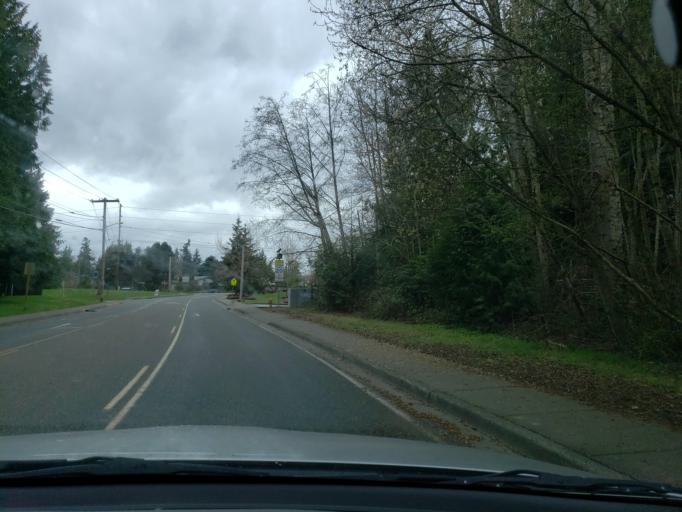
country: US
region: Washington
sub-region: Snohomish County
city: Mukilteo
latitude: 47.8976
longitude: -122.3024
